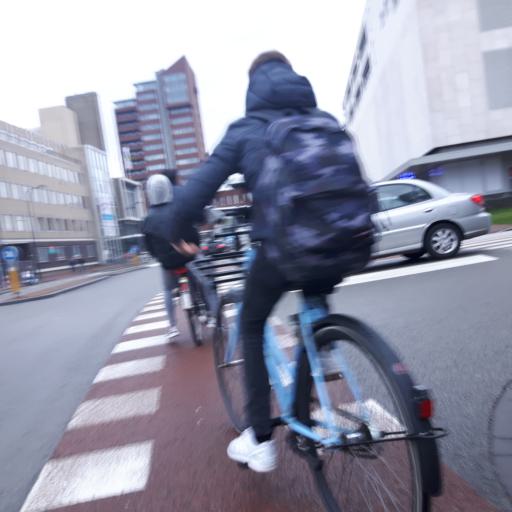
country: NL
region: Overijssel
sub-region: Gemeente Enschede
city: Enschede
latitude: 52.2163
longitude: 6.8961
